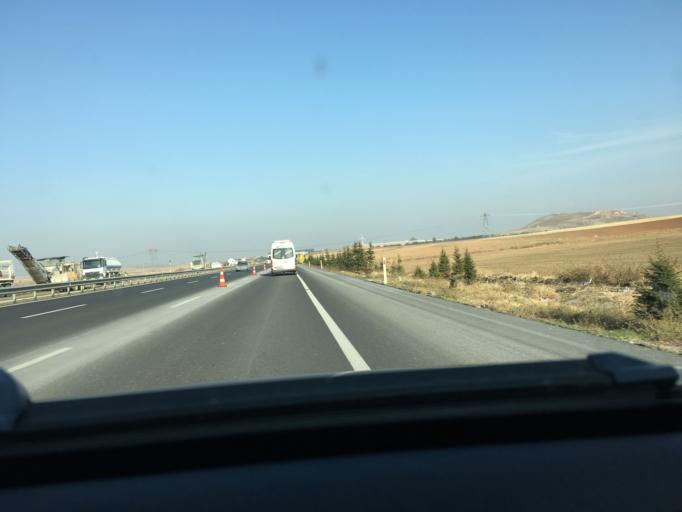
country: TR
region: Ankara
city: Temelli
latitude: 39.7075
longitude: 32.2829
